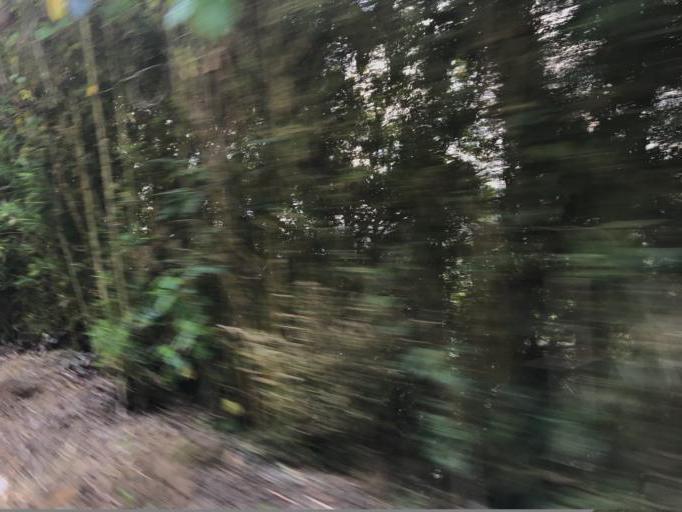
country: CO
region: Valle del Cauca
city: Cali
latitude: 3.4692
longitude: -76.6246
